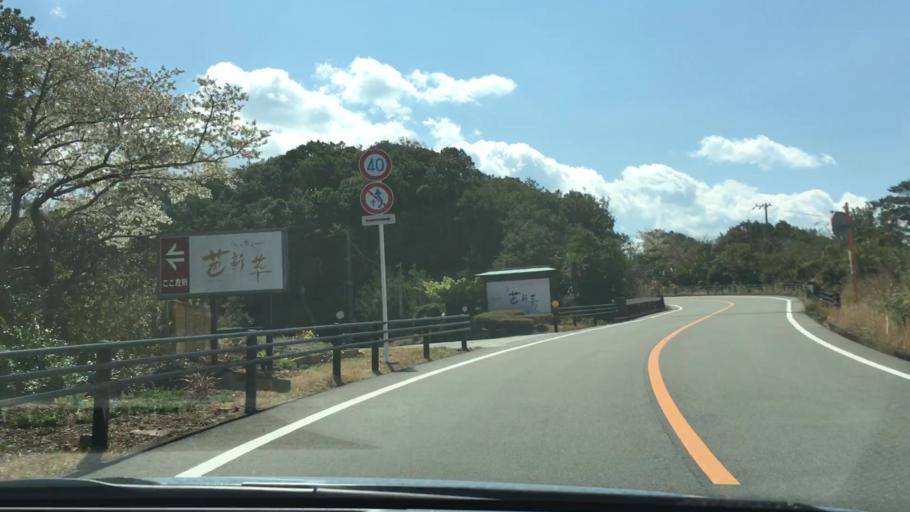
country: JP
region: Mie
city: Toba
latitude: 34.4482
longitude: 136.9110
